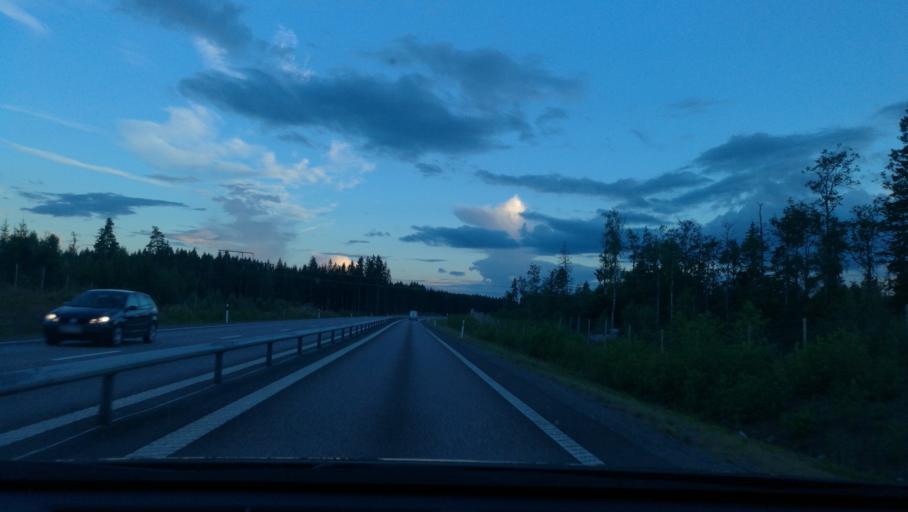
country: SE
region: Soedermanland
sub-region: Katrineholms Kommun
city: Katrineholm
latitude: 58.9485
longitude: 16.2173
